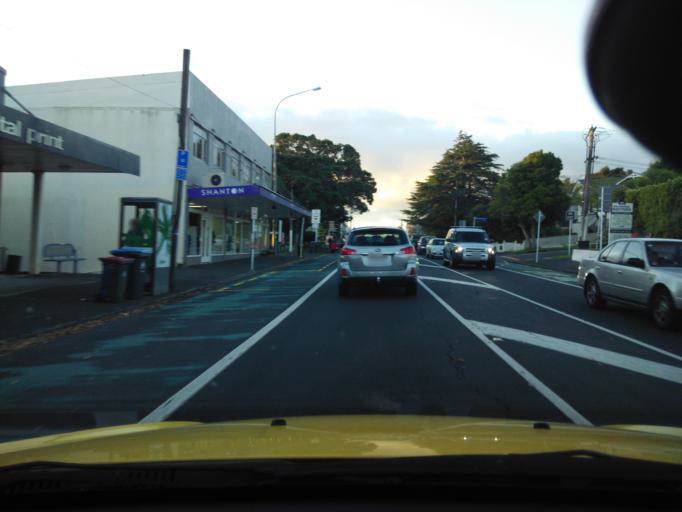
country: NZ
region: Auckland
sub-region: Auckland
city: Auckland
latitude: -36.8847
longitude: 174.7482
